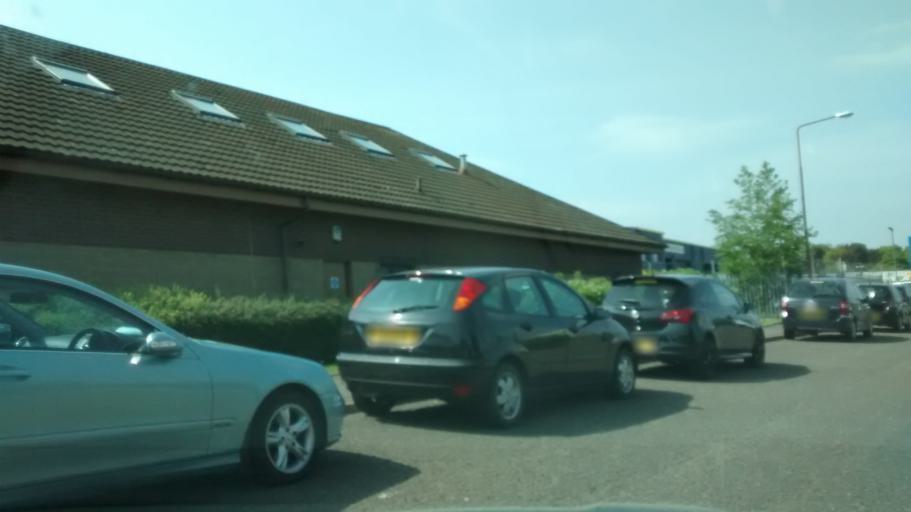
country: GB
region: Scotland
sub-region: West Lothian
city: Mid Calder
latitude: 55.9044
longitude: -3.4967
